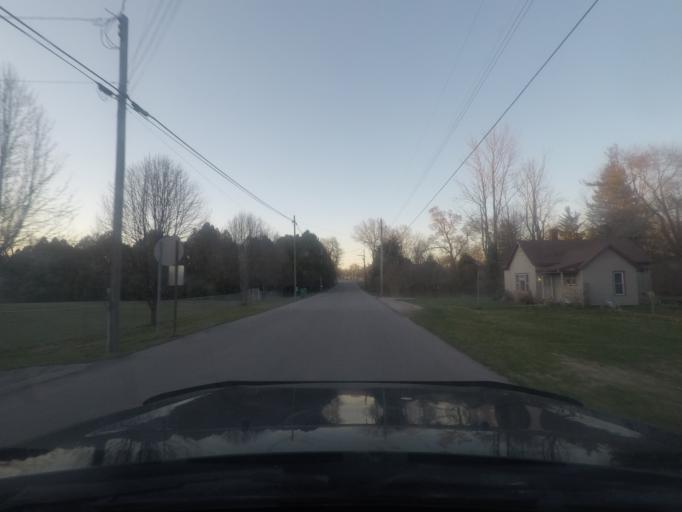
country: US
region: Indiana
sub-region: LaPorte County
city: Kingsford Heights
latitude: 41.5230
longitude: -86.7015
